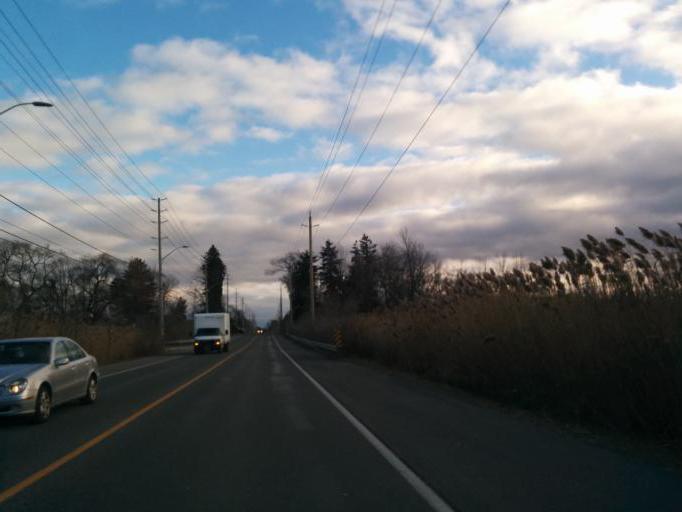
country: CA
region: Ontario
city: Oakville
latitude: 43.4912
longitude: -79.6385
